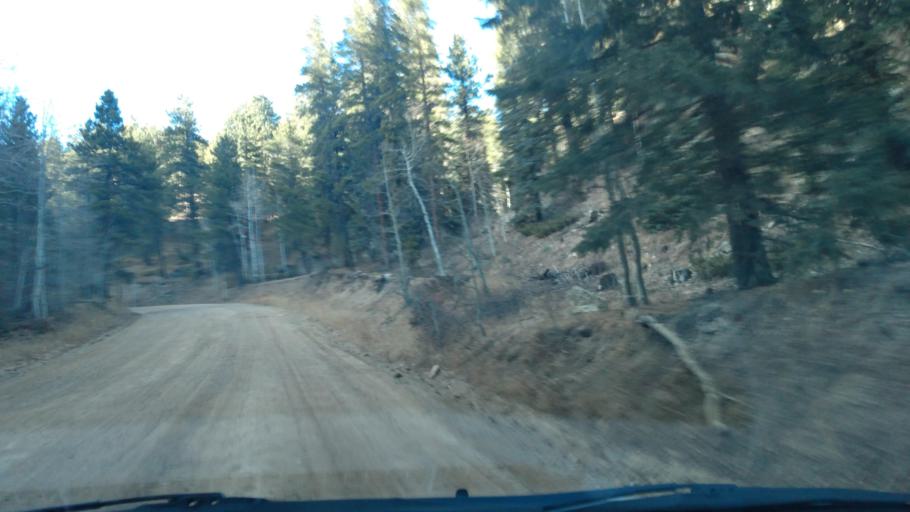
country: US
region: Colorado
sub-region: Boulder County
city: Nederland
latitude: 39.9443
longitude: -105.4451
